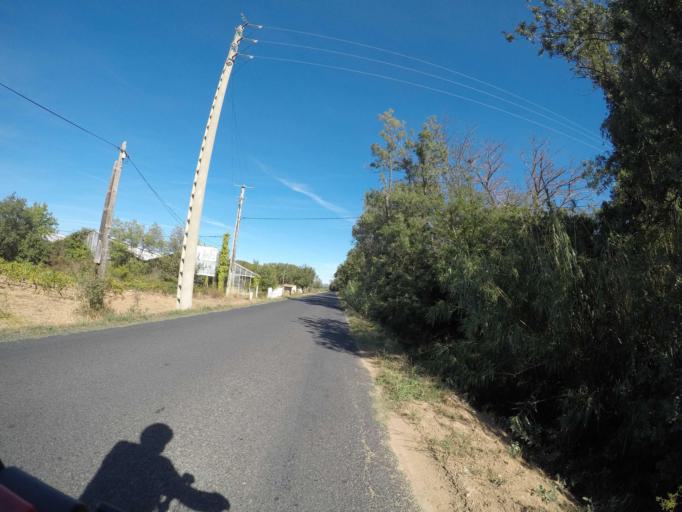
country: FR
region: Languedoc-Roussillon
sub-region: Departement des Pyrenees-Orientales
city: Le Soler
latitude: 42.6586
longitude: 2.7971
